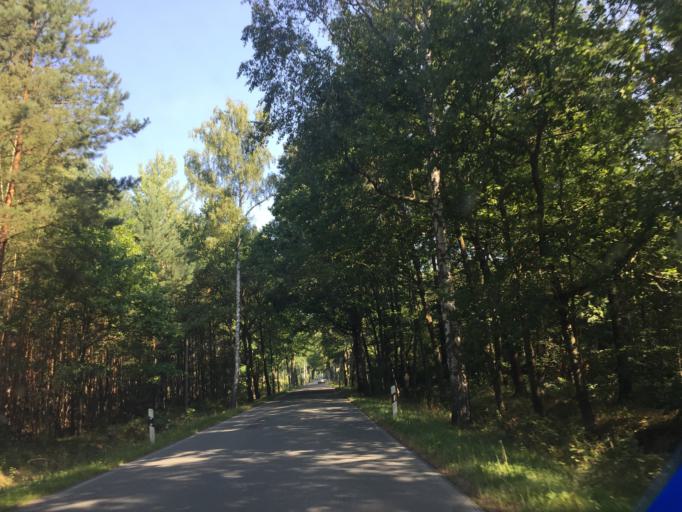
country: DE
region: Saxony
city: Uhyst
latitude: 51.3506
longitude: 14.5059
